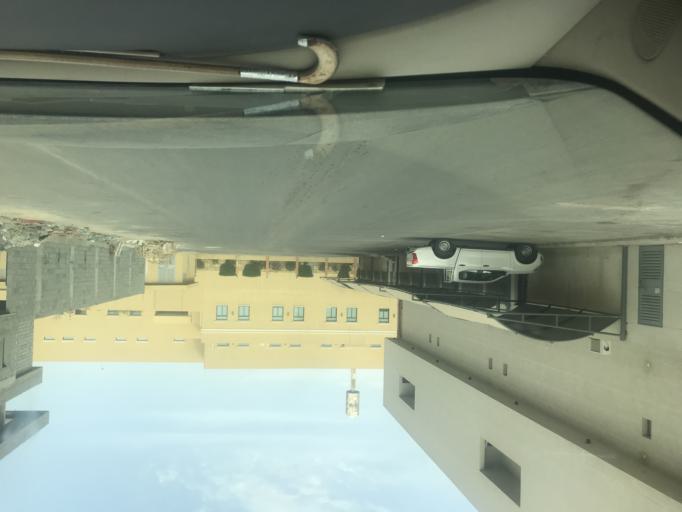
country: SA
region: Ar Riyad
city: Riyadh
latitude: 24.8082
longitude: 46.6675
